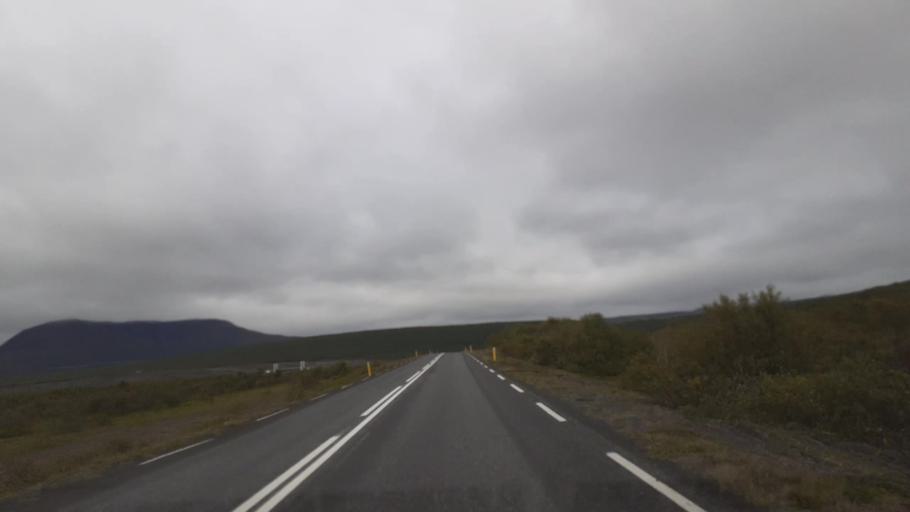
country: IS
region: Northeast
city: Husavik
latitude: 66.0308
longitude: -16.4735
